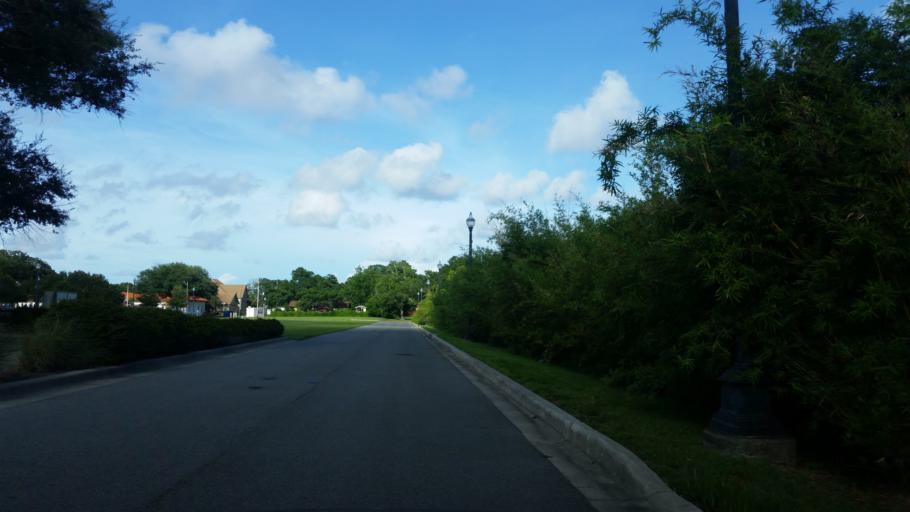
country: US
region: Florida
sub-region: Escambia County
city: Pensacola
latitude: 30.4146
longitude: -87.2069
